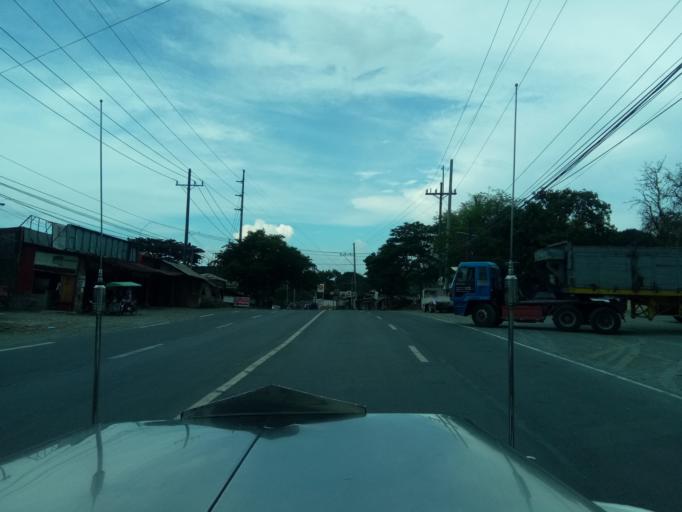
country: PH
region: Calabarzon
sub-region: Province of Cavite
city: Aliang
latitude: 14.2803
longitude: 120.8854
